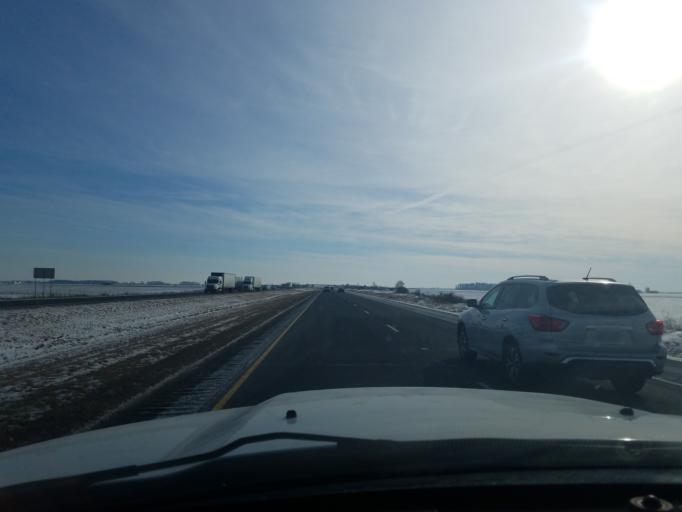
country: US
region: Indiana
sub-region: Huntington County
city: Markle
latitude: 40.8855
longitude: -85.3456
